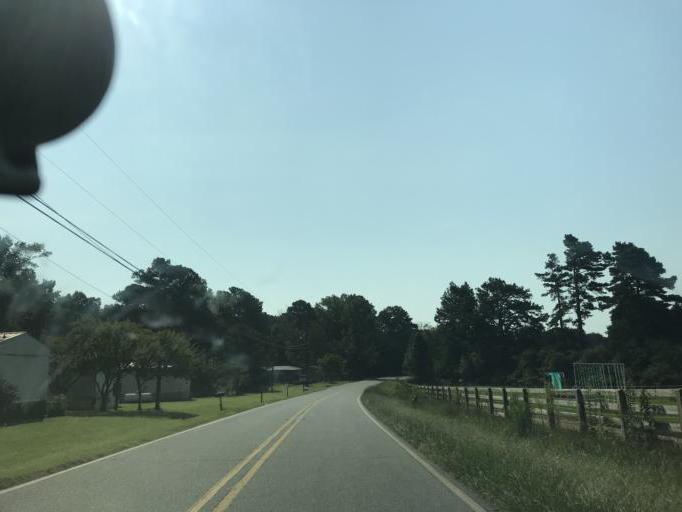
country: US
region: Georgia
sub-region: Forsyth County
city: Cumming
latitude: 34.2450
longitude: -84.1139
